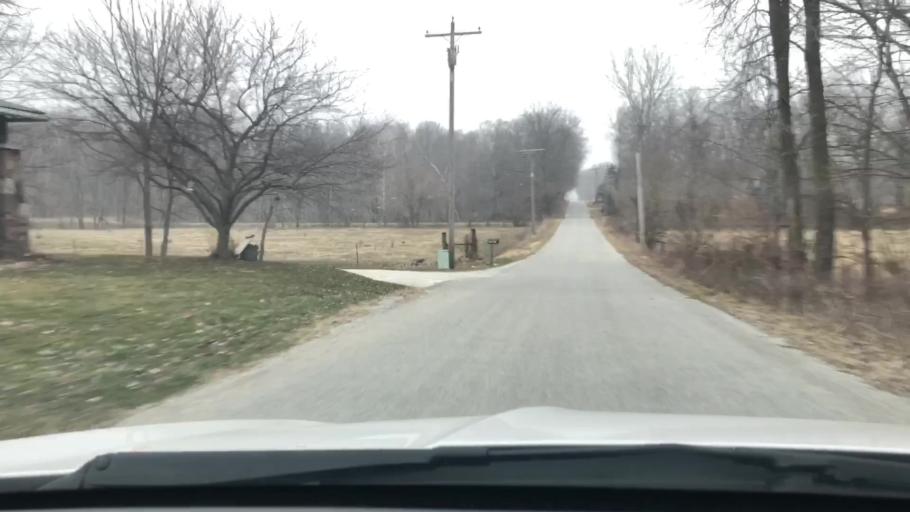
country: US
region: Indiana
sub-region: Fulton County
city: Akron
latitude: 41.0431
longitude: -86.0570
